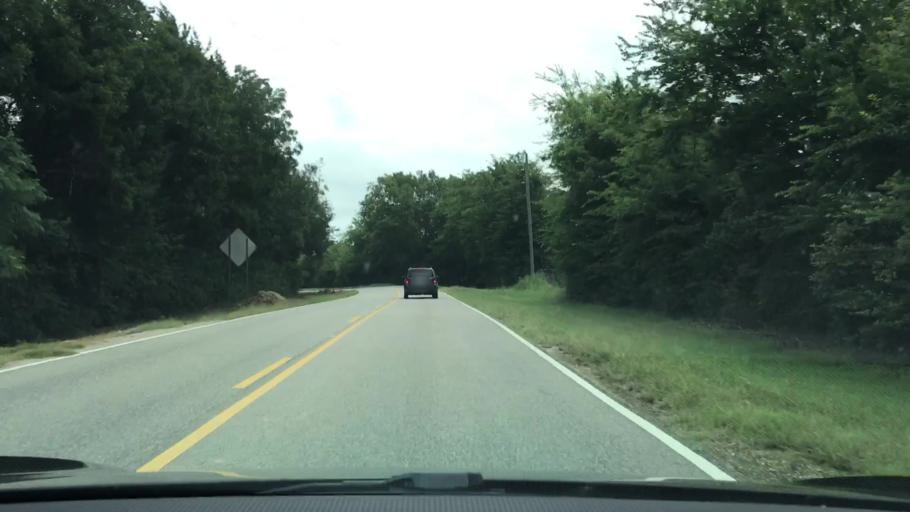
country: US
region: Alabama
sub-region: Montgomery County
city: Pike Road
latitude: 32.2886
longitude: -86.0777
